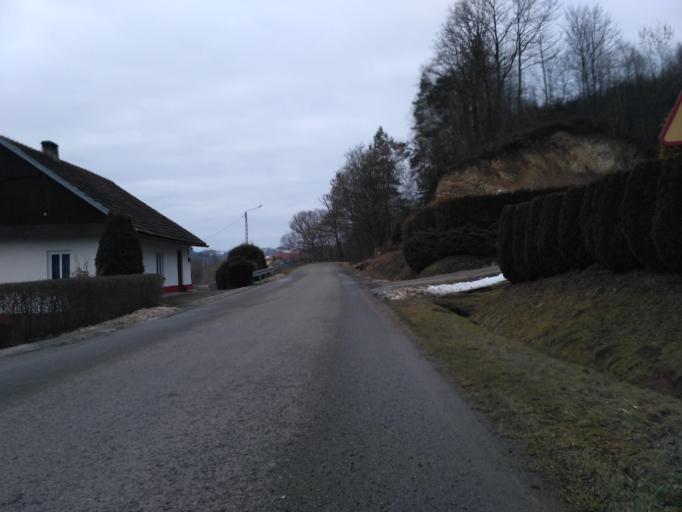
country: PL
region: Subcarpathian Voivodeship
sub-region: Powiat brzozowski
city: Wesola
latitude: 49.7783
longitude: 22.1395
